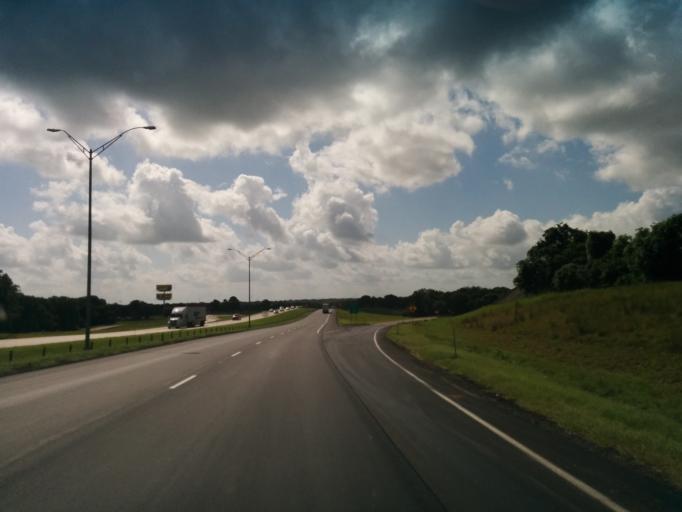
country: US
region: Texas
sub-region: Fayette County
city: Schulenburg
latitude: 29.6957
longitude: -96.8531
